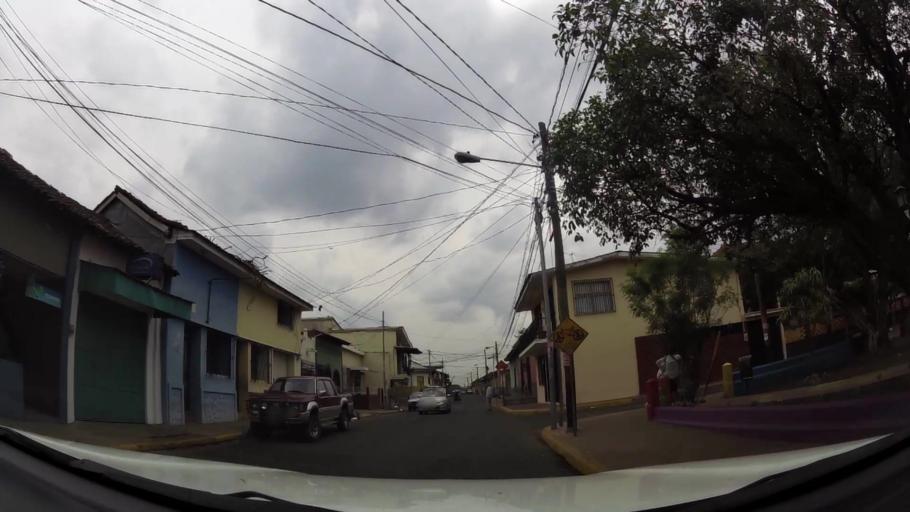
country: NI
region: Leon
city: Leon
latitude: 12.4361
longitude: -86.8737
